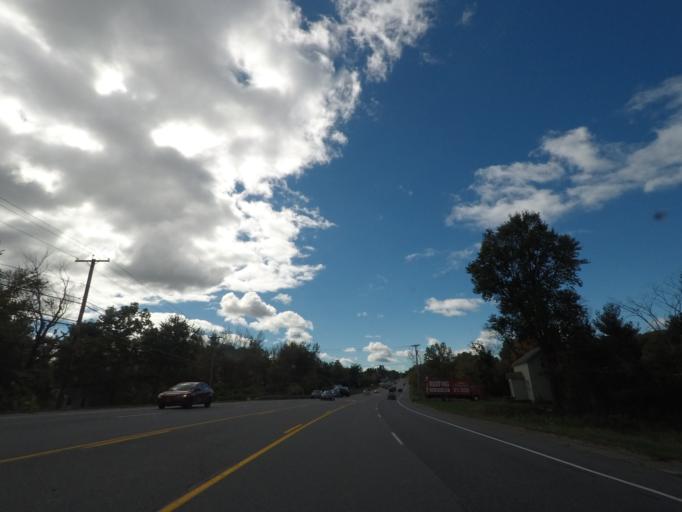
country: US
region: New York
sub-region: Albany County
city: Cohoes
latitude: 42.7935
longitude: -73.7349
